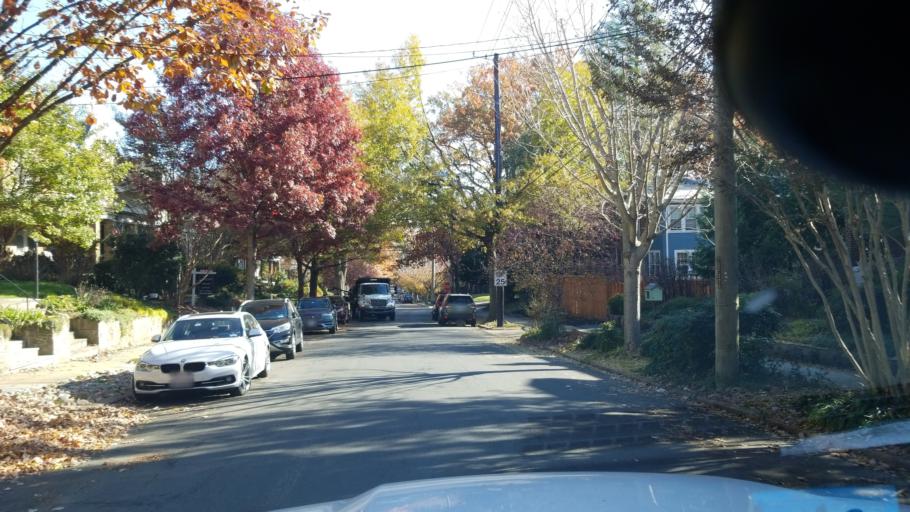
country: US
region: Maryland
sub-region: Montgomery County
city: Friendship Village
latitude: 38.9448
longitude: -77.0755
